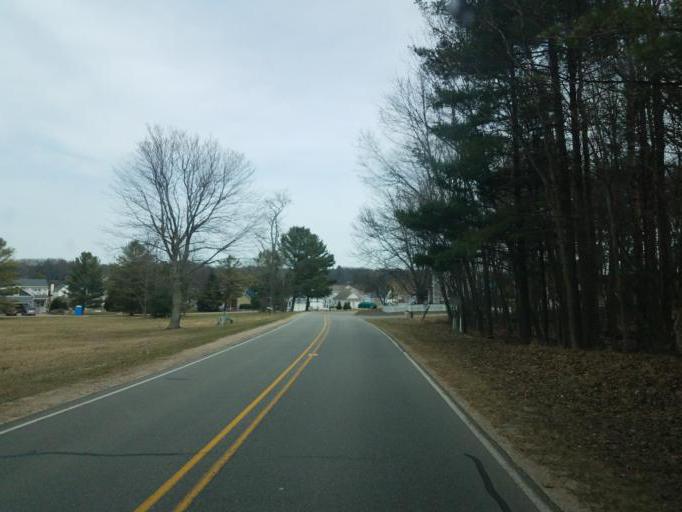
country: US
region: Michigan
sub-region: Oceana County
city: Hart
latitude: 43.7609
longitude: -86.4140
